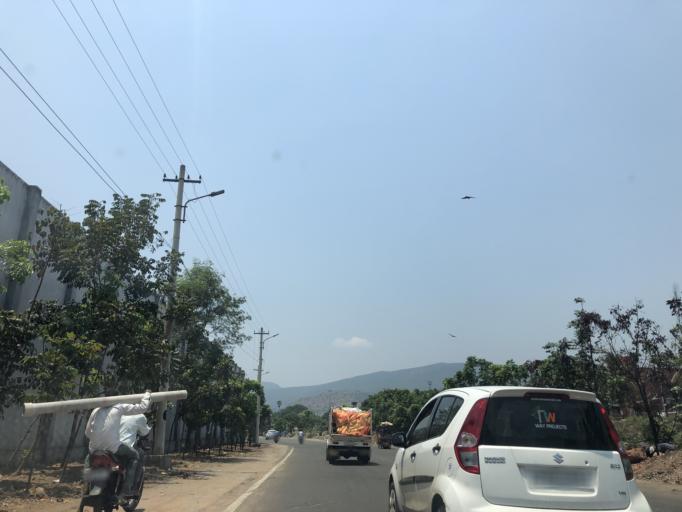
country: IN
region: Andhra Pradesh
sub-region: Vishakhapatnam
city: Yarada
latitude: 17.7154
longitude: 83.2920
